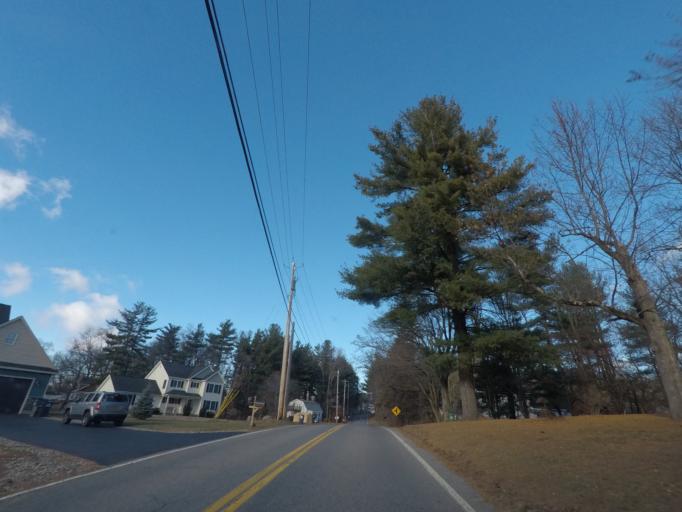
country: US
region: New York
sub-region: Saratoga County
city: Mechanicville
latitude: 42.8754
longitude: -73.7475
